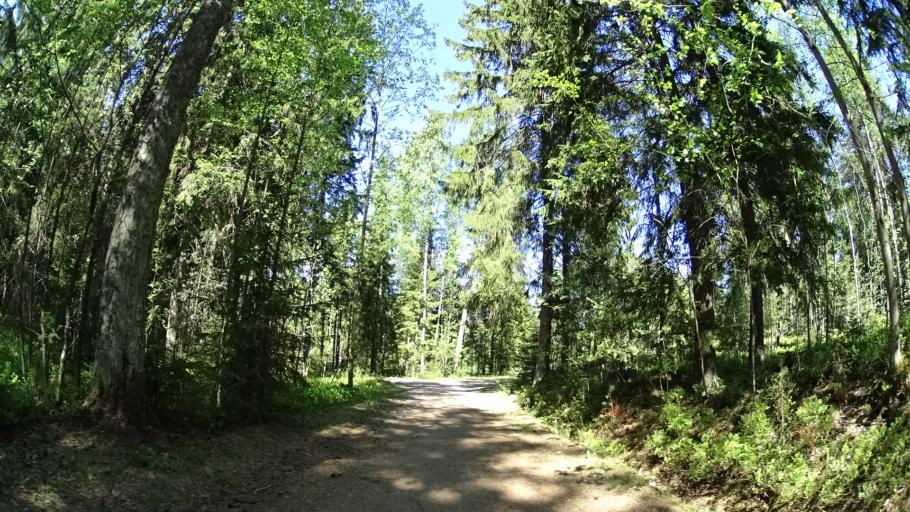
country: FI
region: Uusimaa
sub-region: Helsinki
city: Espoo
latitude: 60.1734
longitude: 24.6250
